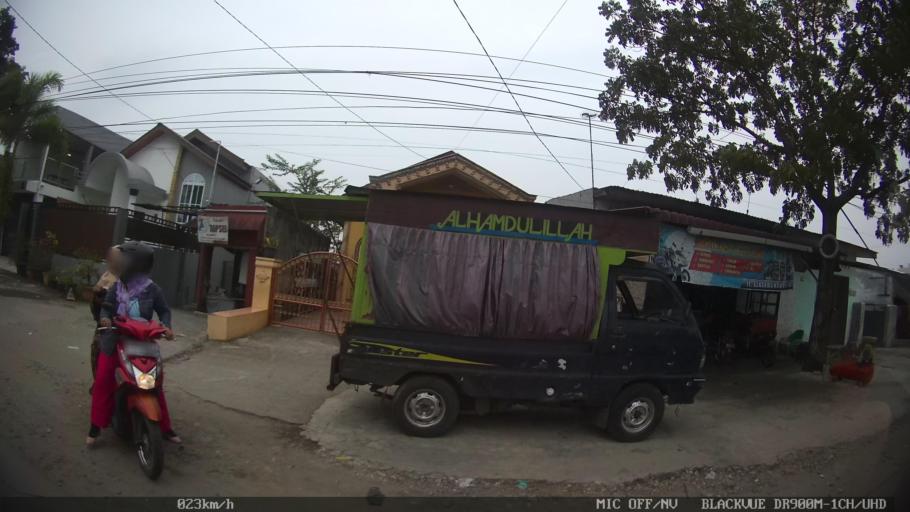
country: ID
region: North Sumatra
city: Medan
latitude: 3.5526
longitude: 98.7058
